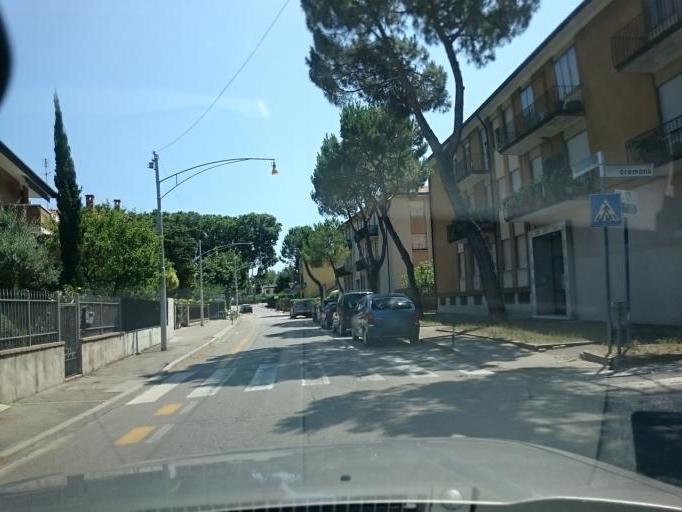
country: IT
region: Veneto
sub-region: Provincia di Padova
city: Padova
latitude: 45.4005
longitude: 11.8619
